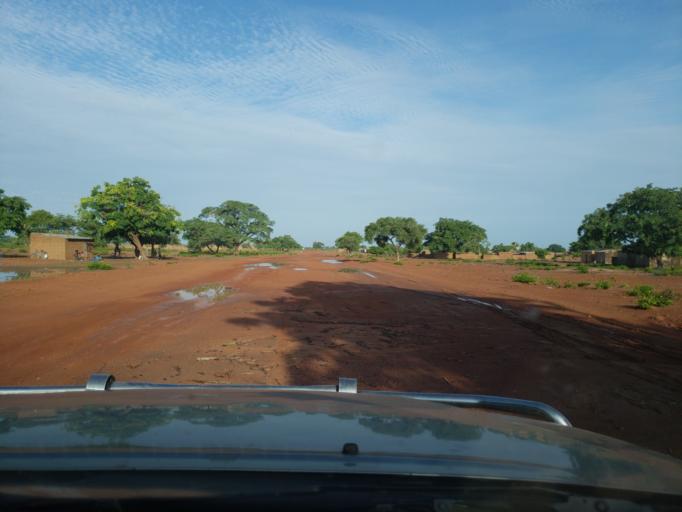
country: ML
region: Sikasso
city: Koutiala
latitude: 12.4289
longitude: -5.6186
